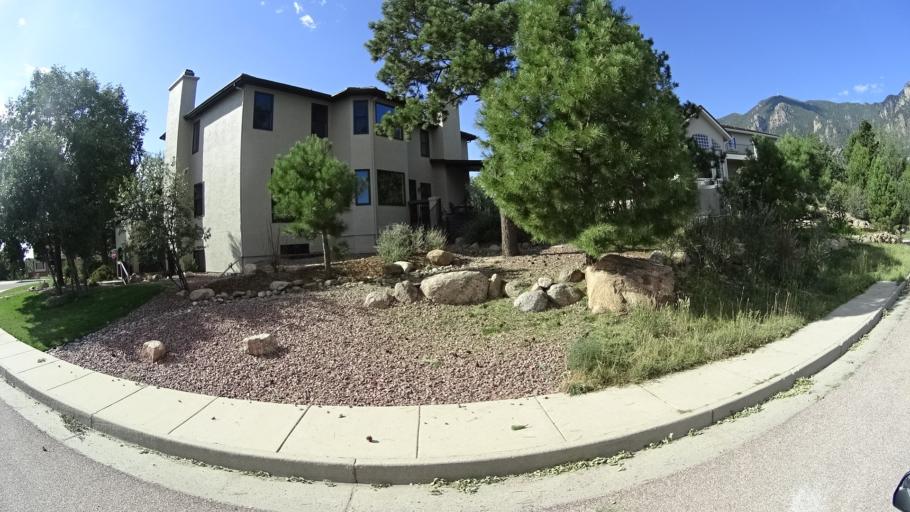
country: US
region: Colorado
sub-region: El Paso County
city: Stratmoor
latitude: 38.7675
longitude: -104.8306
